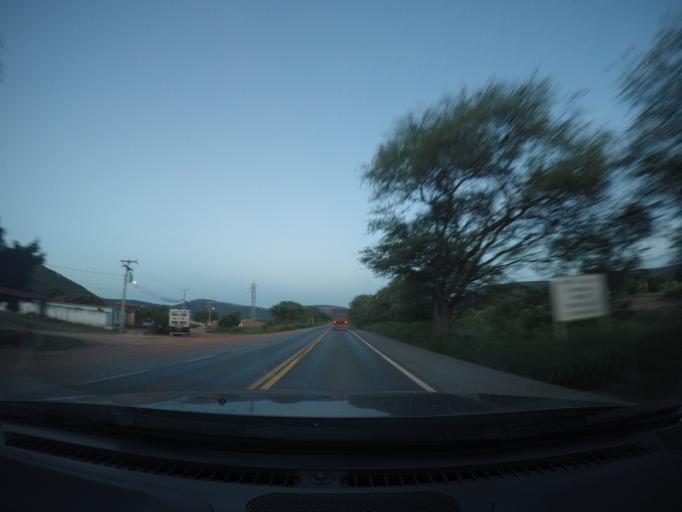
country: BR
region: Bahia
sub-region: Seabra
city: Seabra
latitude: -12.4873
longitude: -41.7273
